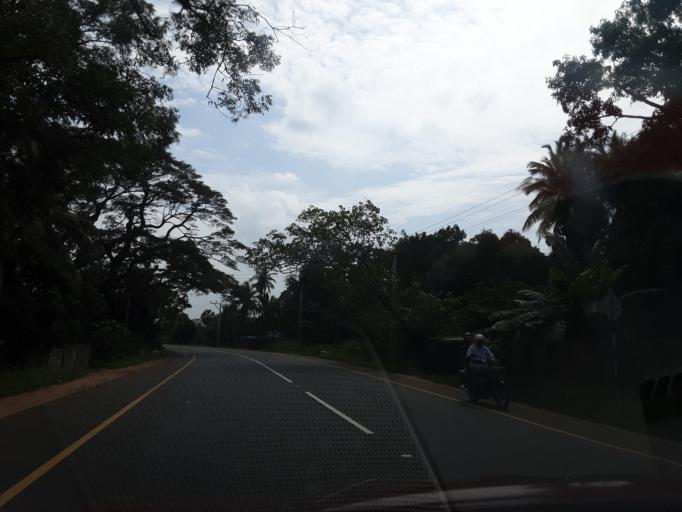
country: LK
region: North Central
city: Anuradhapura
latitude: 8.5183
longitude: 80.5024
